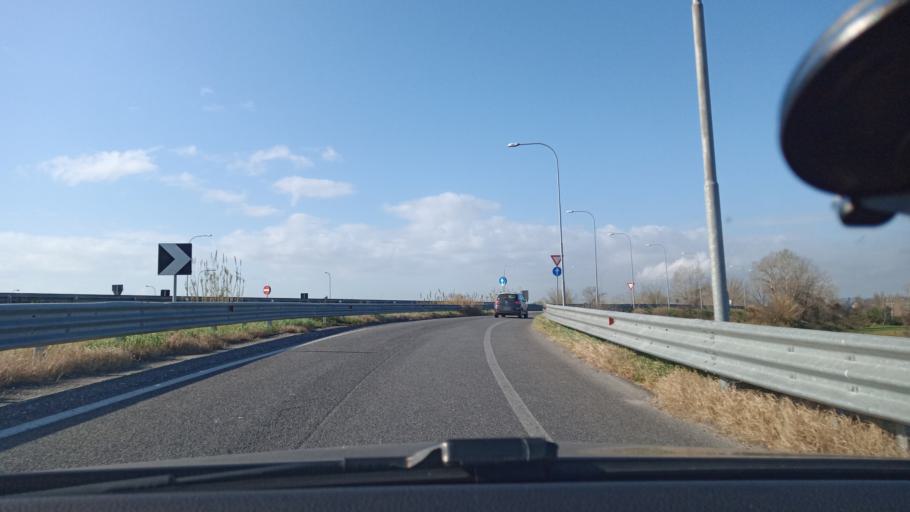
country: IT
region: Latium
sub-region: Citta metropolitana di Roma Capitale
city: Fiano Romano
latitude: 42.1534
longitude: 12.6414
